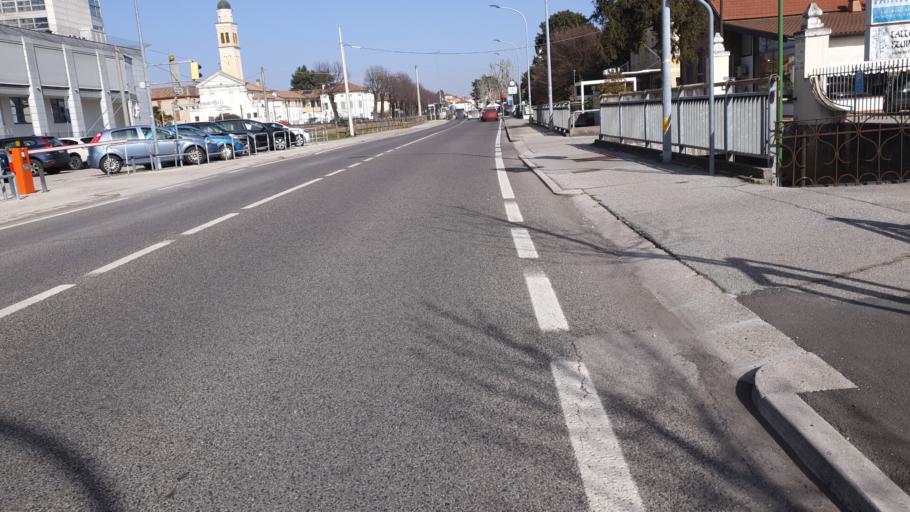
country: IT
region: Veneto
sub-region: Provincia di Padova
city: Camposampiero
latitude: 45.5643
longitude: 11.9302
